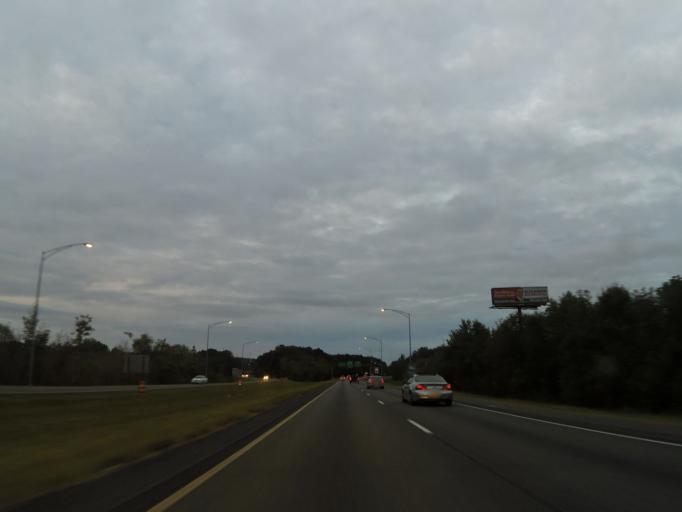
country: US
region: Alabama
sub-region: Etowah County
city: Attalla
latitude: 33.9991
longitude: -86.0857
